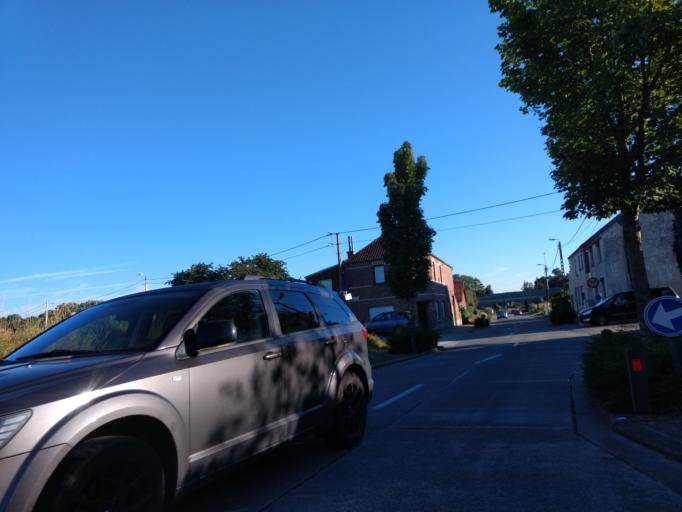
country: BE
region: Flanders
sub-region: Provincie Vlaams-Brabant
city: Bierbeek
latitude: 50.8387
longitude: 4.7503
